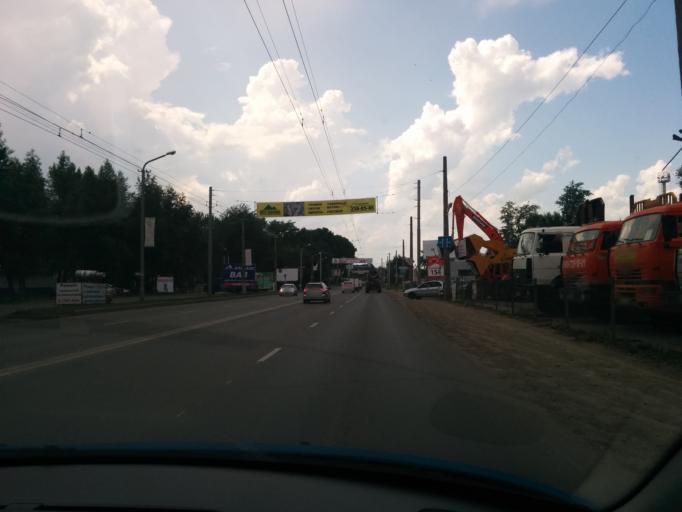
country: RU
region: Perm
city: Kondratovo
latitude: 57.9757
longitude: 56.1629
